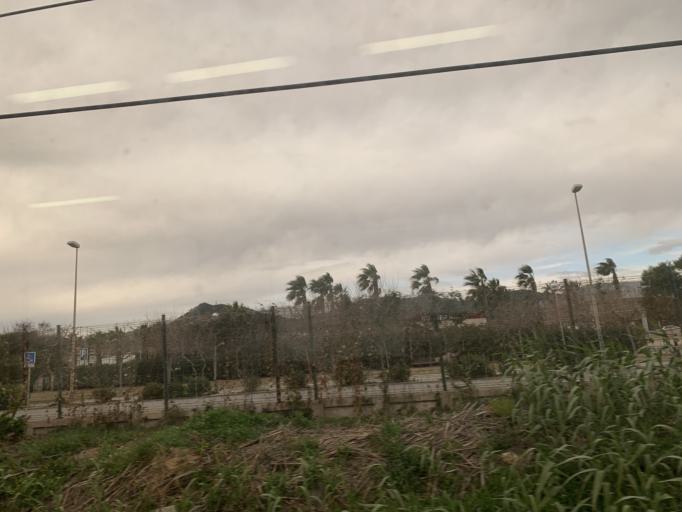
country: ES
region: Catalonia
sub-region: Provincia de Barcelona
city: Cabrera de Mar
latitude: 41.5147
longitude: 2.4148
